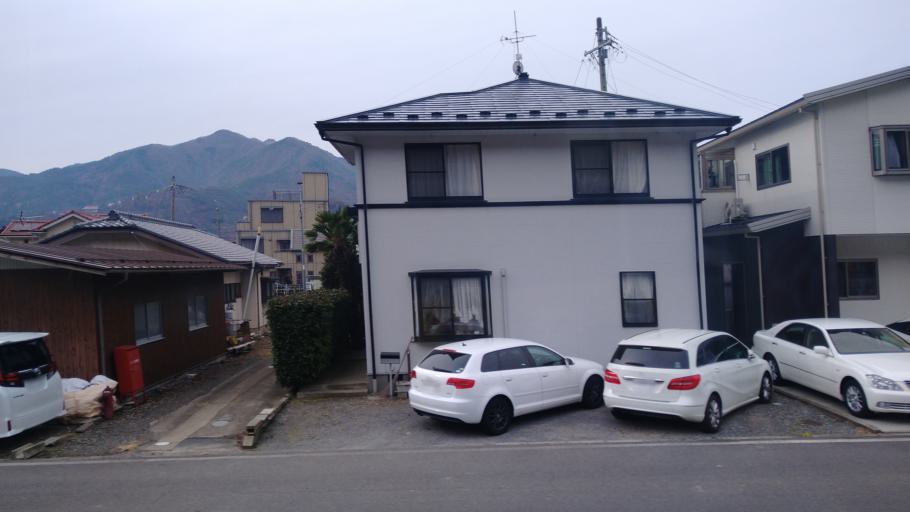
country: JP
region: Nagano
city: Ueda
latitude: 36.4899
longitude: 138.1540
